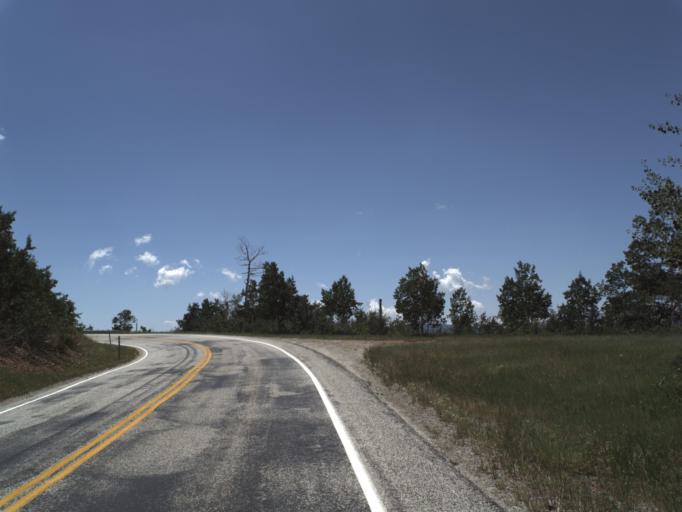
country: US
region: Utah
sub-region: Weber County
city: Wolf Creek
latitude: 41.4226
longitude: -111.5635
